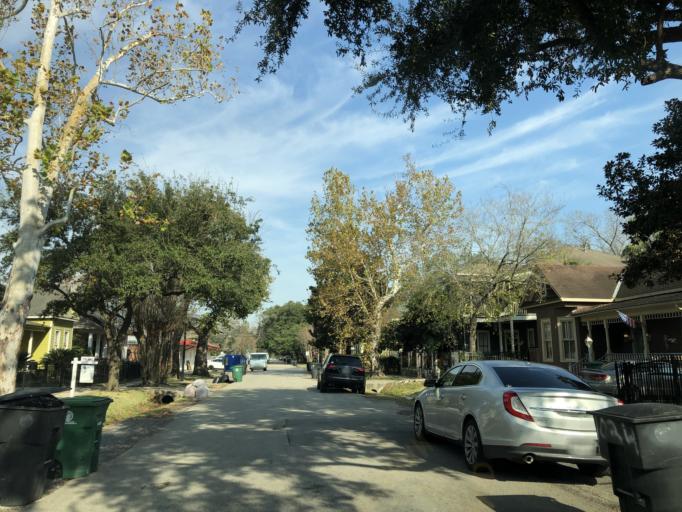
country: US
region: Texas
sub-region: Harris County
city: Houston
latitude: 29.7897
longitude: -95.3942
